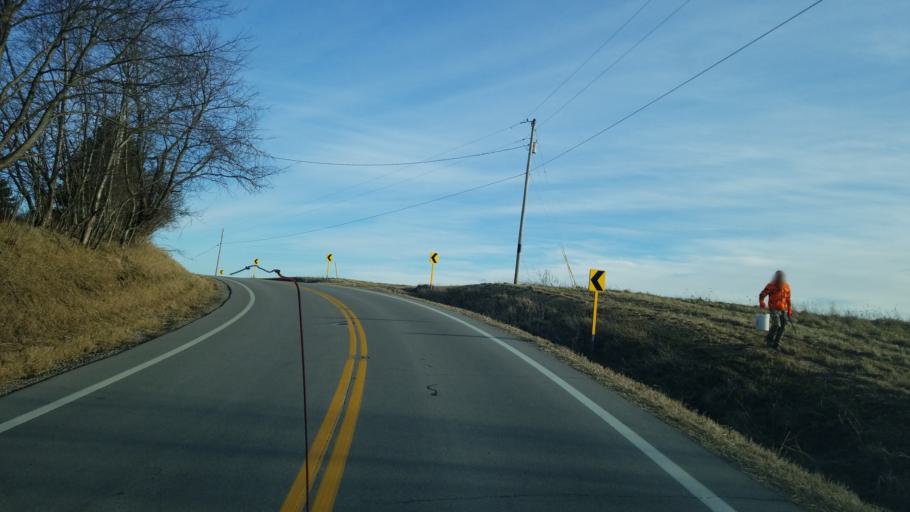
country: US
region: Ohio
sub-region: Huron County
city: Greenwich
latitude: 41.1015
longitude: -82.5303
